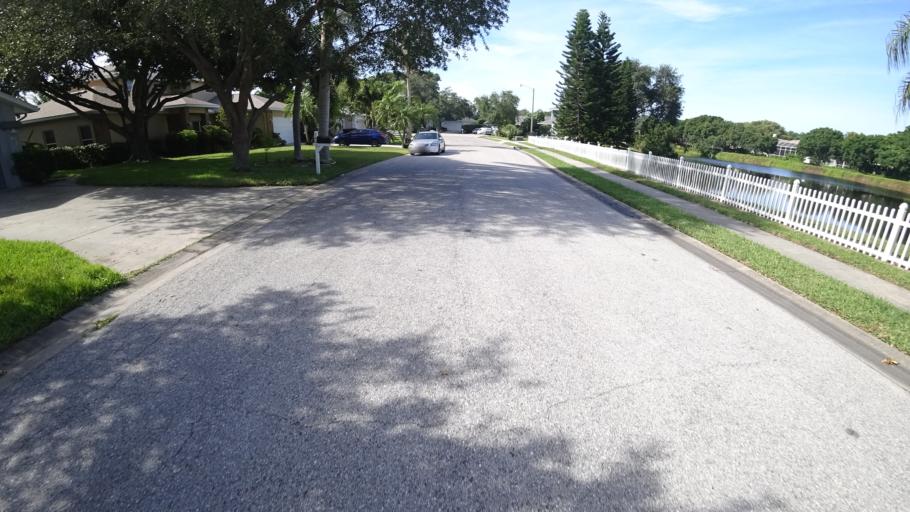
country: US
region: Florida
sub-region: Manatee County
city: West Bradenton
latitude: 27.5121
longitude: -82.6532
